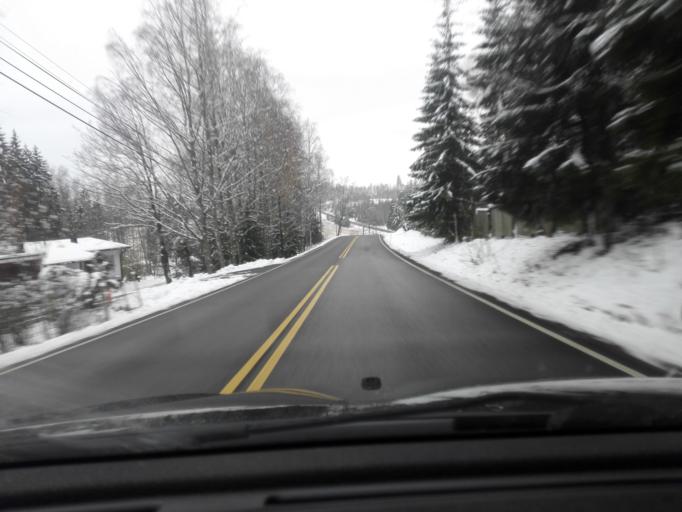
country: FI
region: Uusimaa
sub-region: Helsinki
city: Vihti
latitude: 60.4172
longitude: 24.4051
